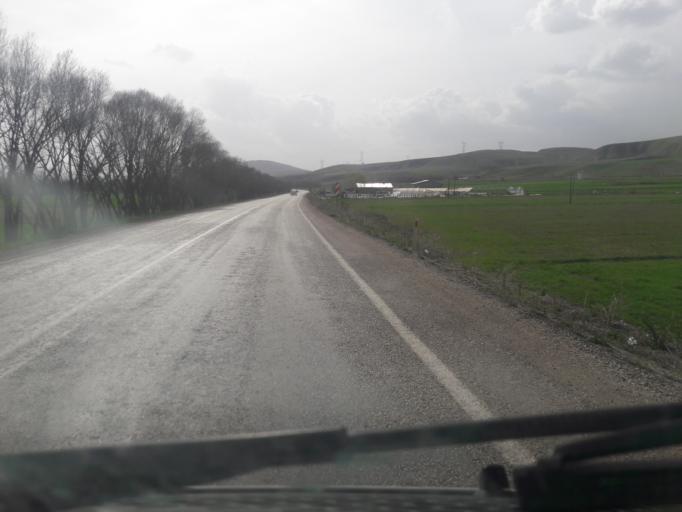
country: TR
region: Gumushane
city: Kelkit
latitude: 40.1428
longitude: 39.4201
